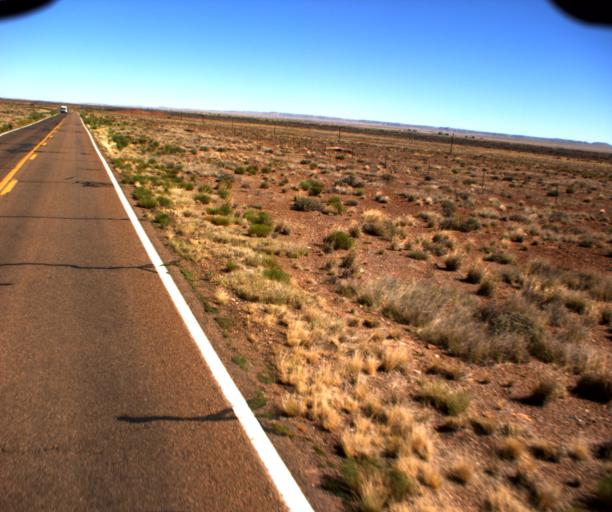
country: US
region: Arizona
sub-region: Coconino County
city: LeChee
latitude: 35.2855
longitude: -110.9836
